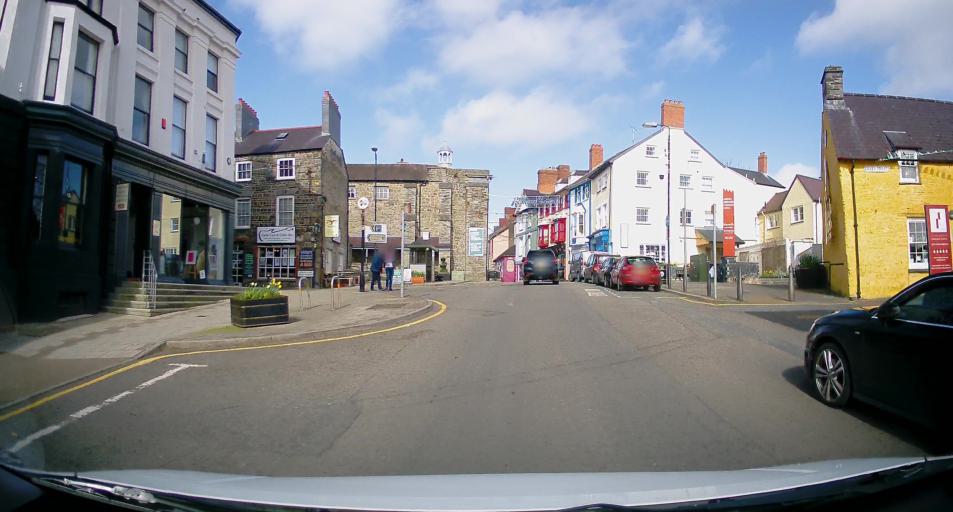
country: GB
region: Wales
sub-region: County of Ceredigion
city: Cardigan
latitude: 52.0815
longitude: -4.6614
